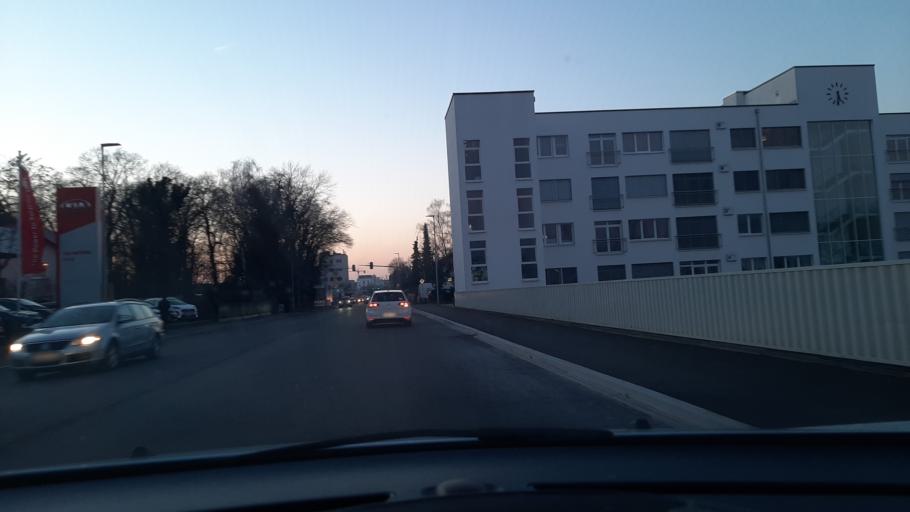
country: DE
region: Baden-Wuerttemberg
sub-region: Regierungsbezirk Stuttgart
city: Eislingen
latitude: 48.6921
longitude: 9.7153
